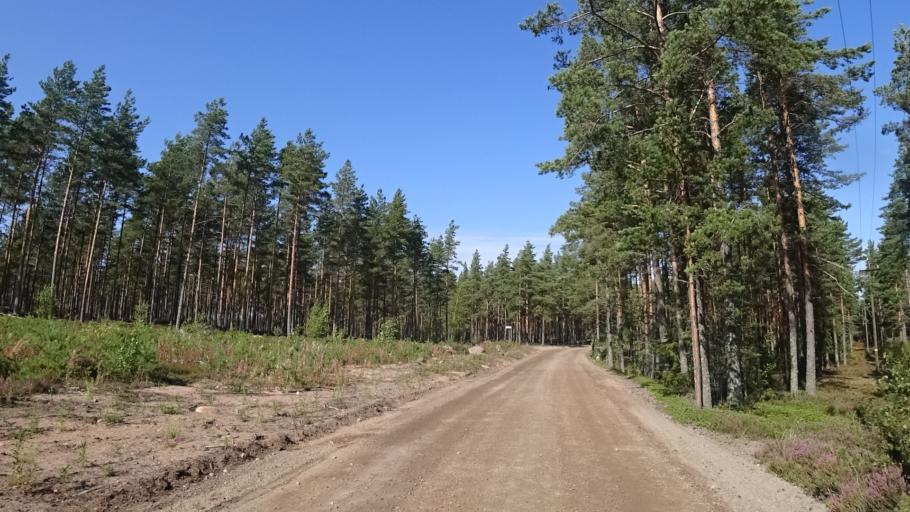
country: FI
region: Kymenlaakso
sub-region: Kotka-Hamina
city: Hamina
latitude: 60.5471
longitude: 27.2124
